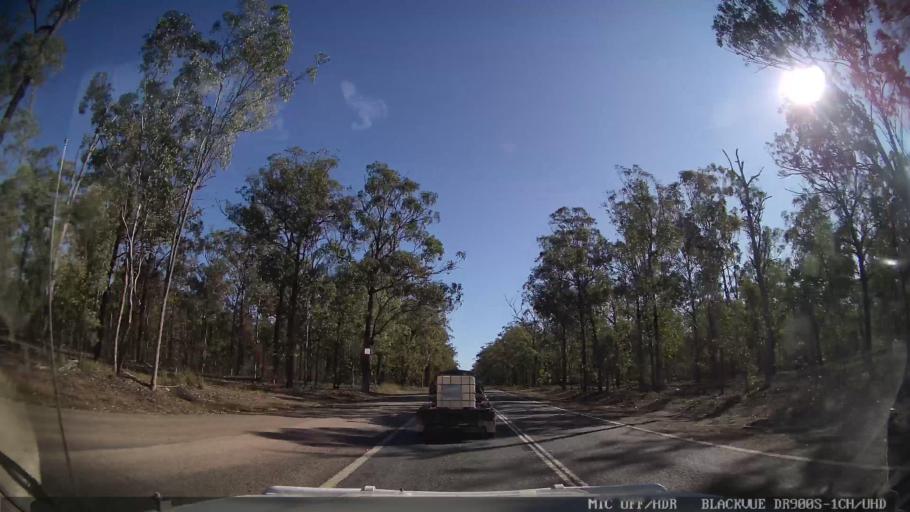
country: AU
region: Queensland
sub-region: Bundaberg
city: Childers
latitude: -25.2163
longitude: 152.0742
